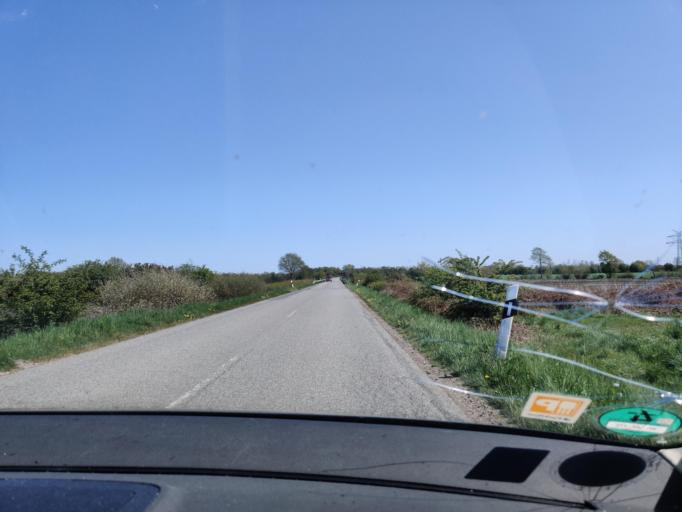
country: DE
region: Schleswig-Holstein
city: Sankelmark
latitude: 54.7107
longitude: 9.3754
